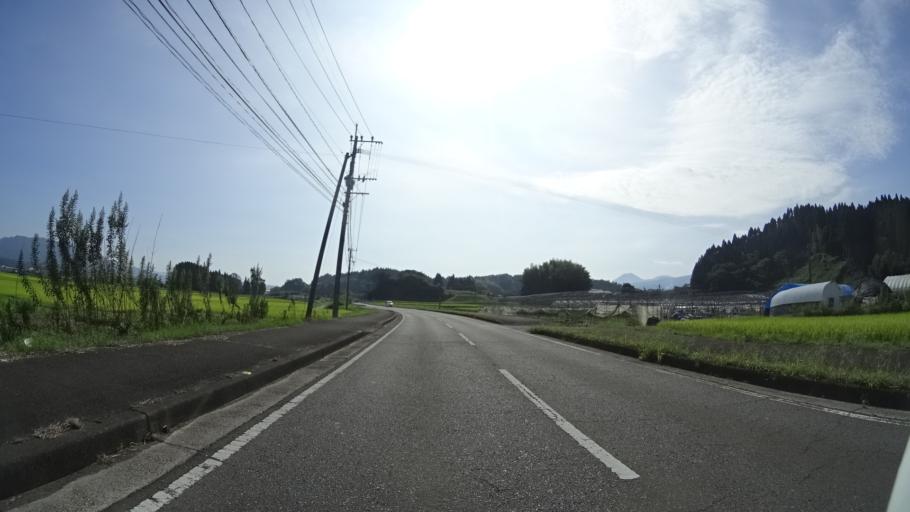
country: JP
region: Miyazaki
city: Kobayashi
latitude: 32.0375
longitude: 130.8075
